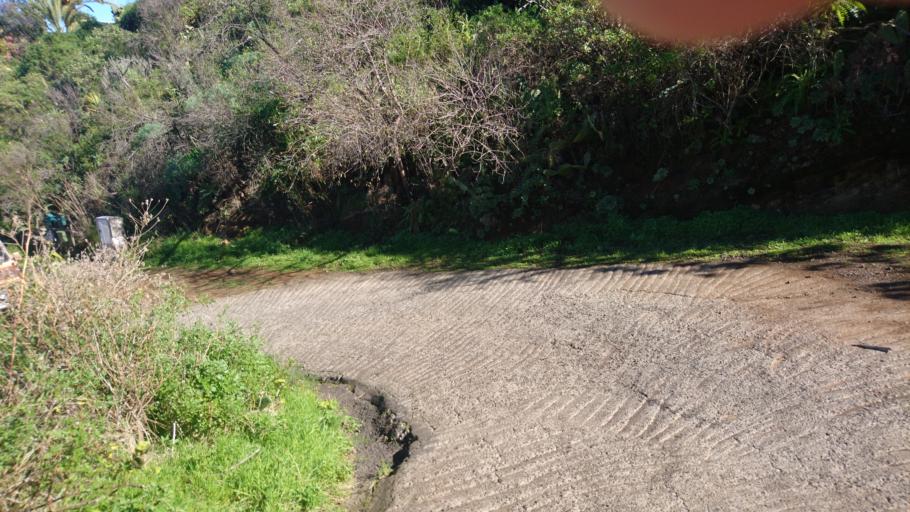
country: ES
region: Canary Islands
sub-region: Provincia de Santa Cruz de Tenerife
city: Puntagorda
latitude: 28.7896
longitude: -17.9752
